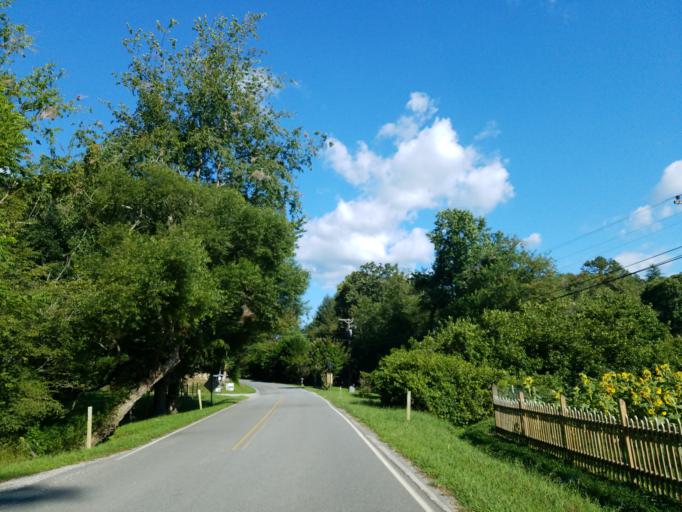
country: US
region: Georgia
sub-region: Fannin County
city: Blue Ridge
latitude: 34.7594
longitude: -84.2152
